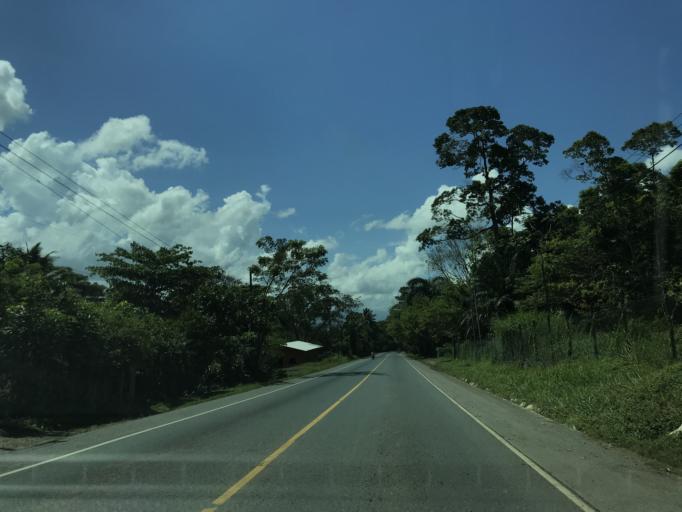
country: GT
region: Izabal
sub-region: Municipio de Puerto Barrios
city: Puerto Barrios
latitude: 15.6602
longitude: -88.5494
